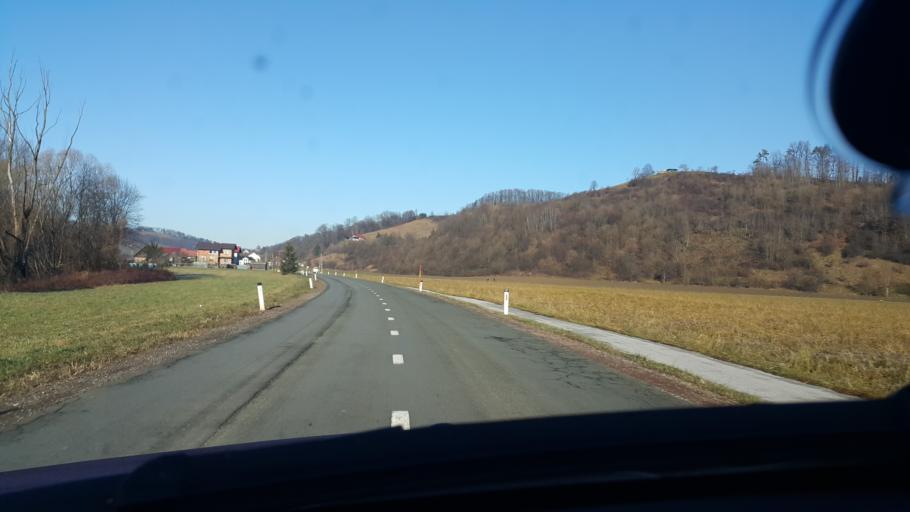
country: SI
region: Kungota
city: Zgornja Kungota
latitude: 46.6250
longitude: 15.6321
